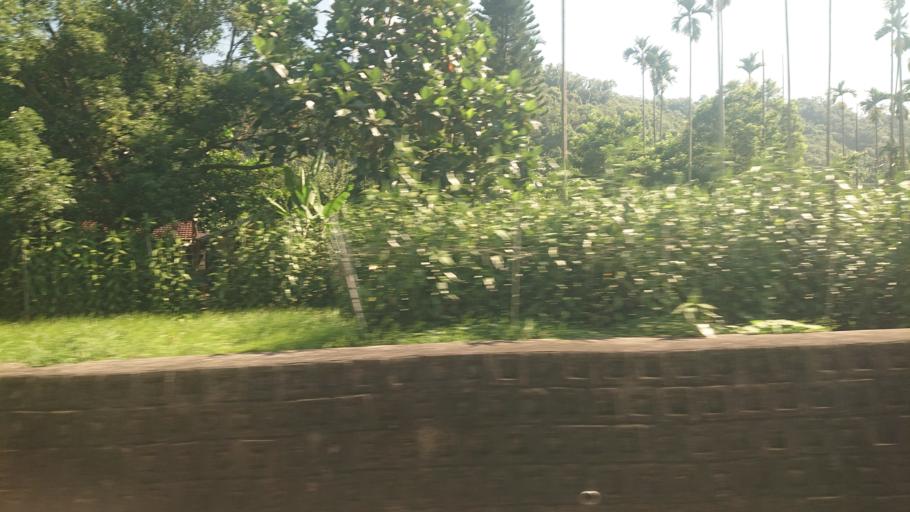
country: TW
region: Taiwan
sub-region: Nantou
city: Puli
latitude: 24.0586
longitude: 120.9028
